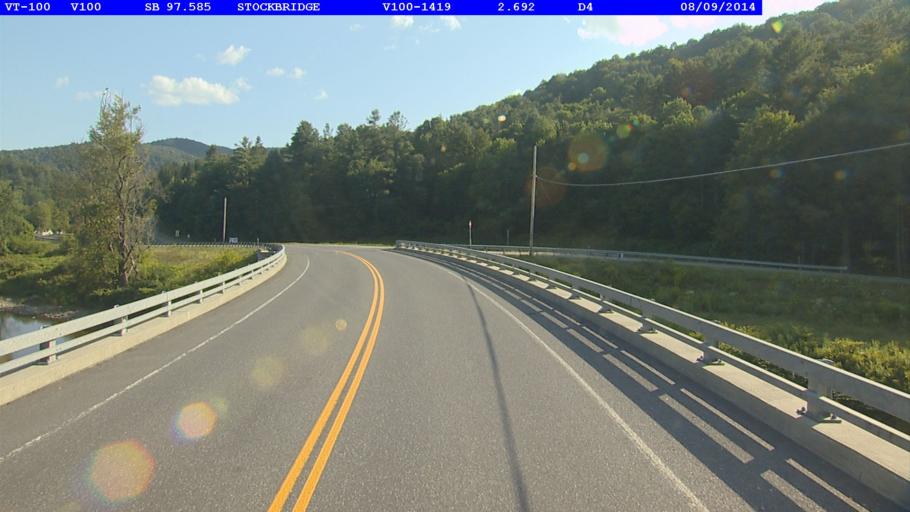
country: US
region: Vermont
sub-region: Orange County
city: Randolph
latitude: 43.7820
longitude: -72.7573
